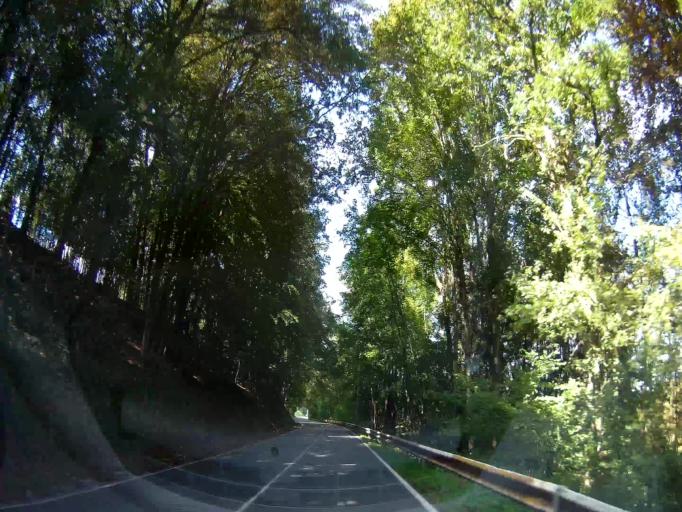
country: BE
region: Wallonia
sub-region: Province du Luxembourg
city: La Roche-en-Ardenne
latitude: 50.1941
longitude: 5.5394
